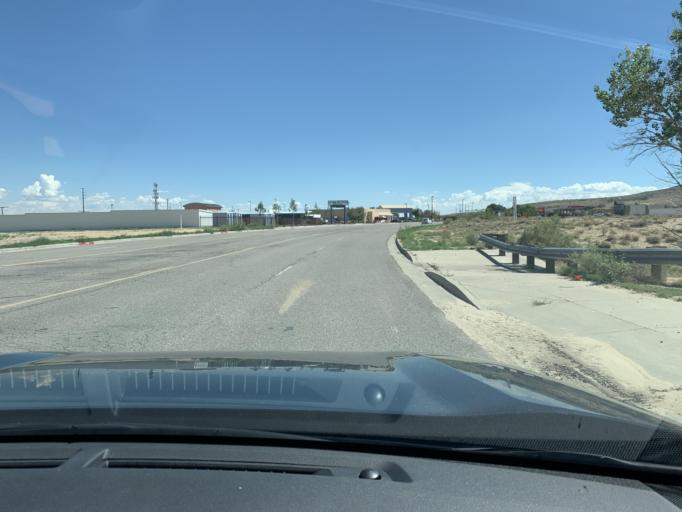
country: US
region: New Mexico
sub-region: Valencia County
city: Los Lunas
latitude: 34.8204
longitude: -106.7683
